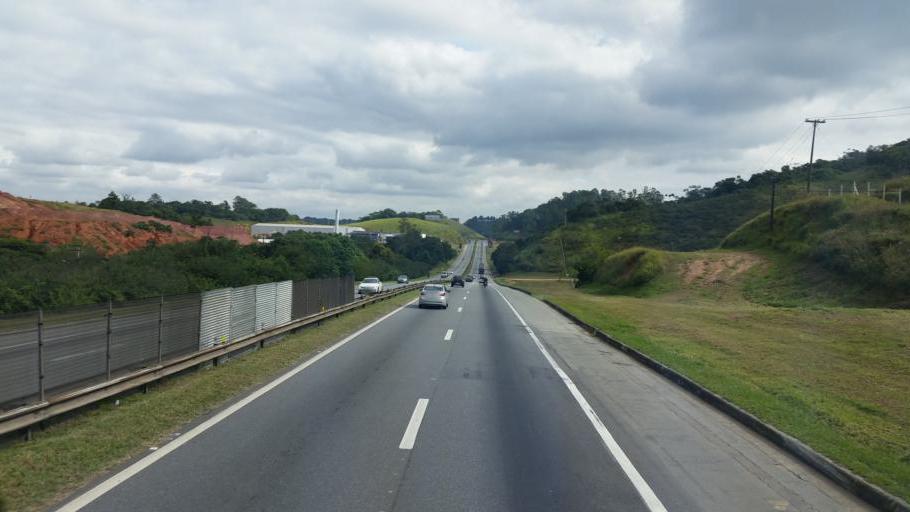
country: BR
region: Sao Paulo
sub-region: Santa Isabel
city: Santa Isabel
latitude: -23.3649
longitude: -46.2265
